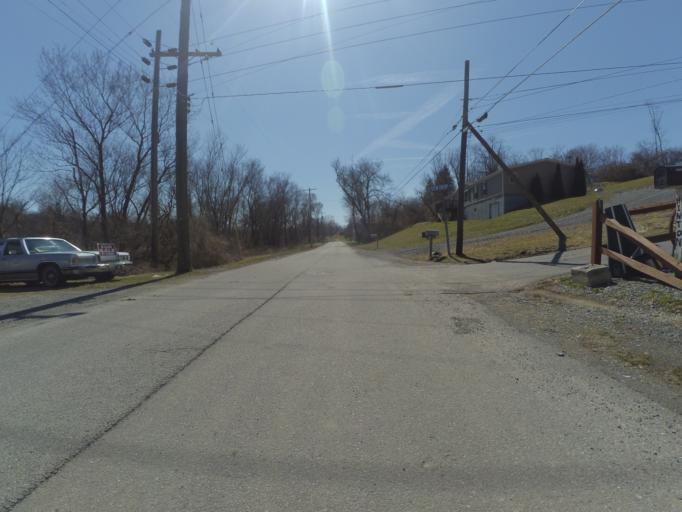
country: US
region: Pennsylvania
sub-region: Centre County
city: Bellefonte
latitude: 40.9202
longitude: -77.7879
